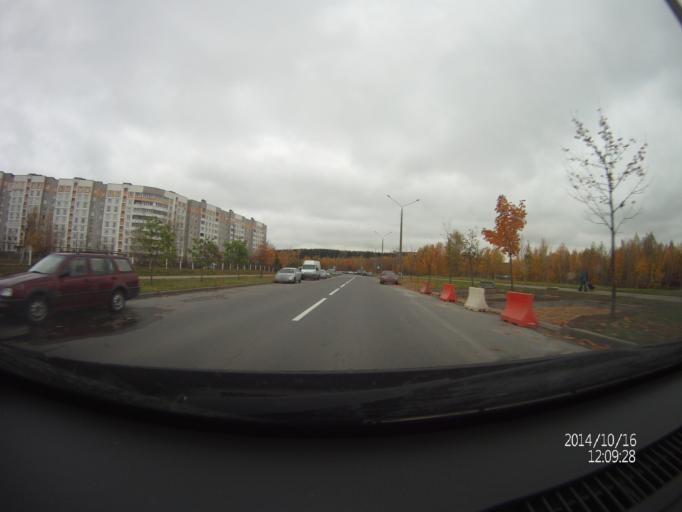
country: BY
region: Minsk
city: Borovlyany
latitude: 53.9355
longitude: 27.6811
